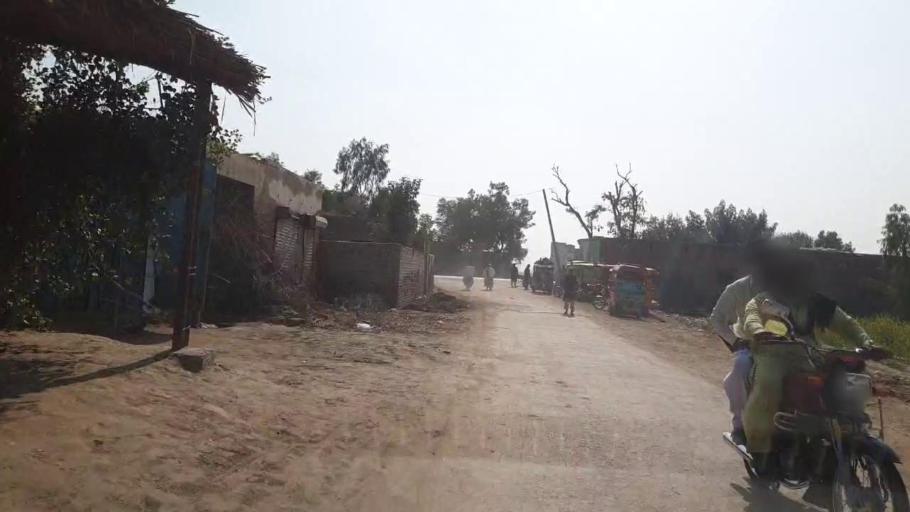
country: PK
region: Sindh
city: Bhit Shah
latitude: 25.6963
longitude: 68.5431
